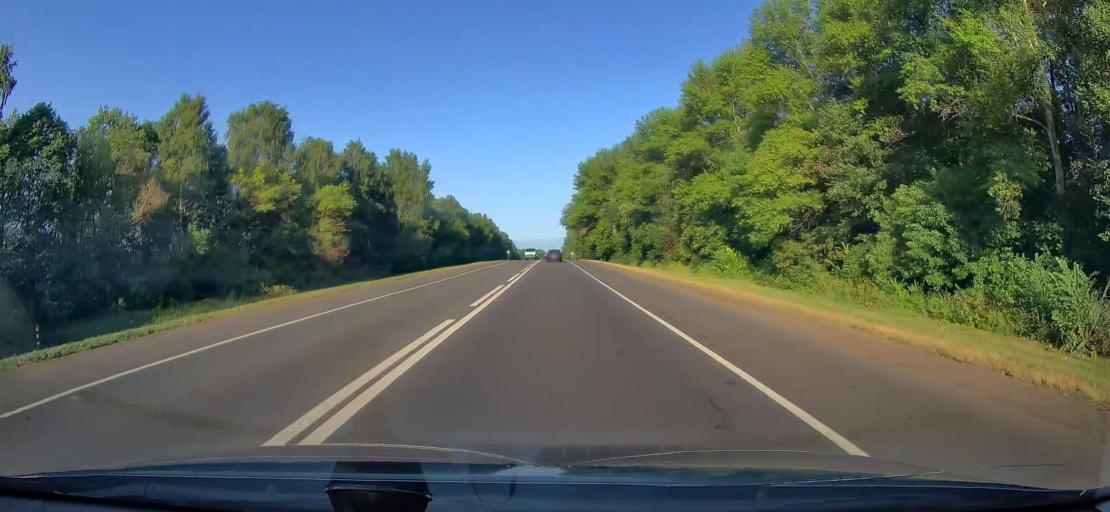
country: RU
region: Tula
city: Plavsk
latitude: 53.6814
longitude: 37.2599
